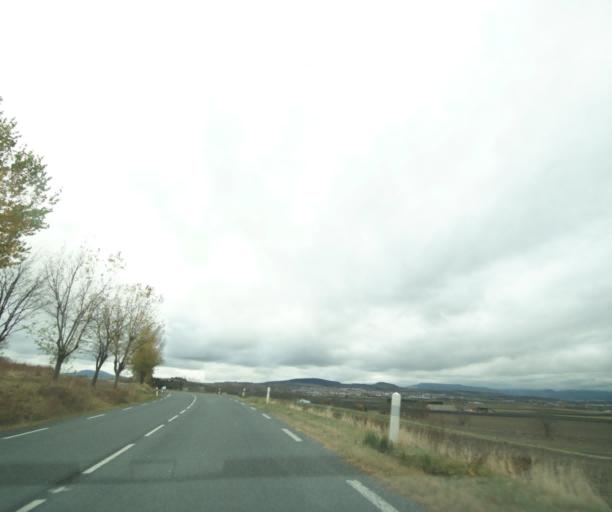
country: FR
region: Auvergne
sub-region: Departement du Puy-de-Dome
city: Pont-du-Chateau
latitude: 45.8033
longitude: 3.2265
